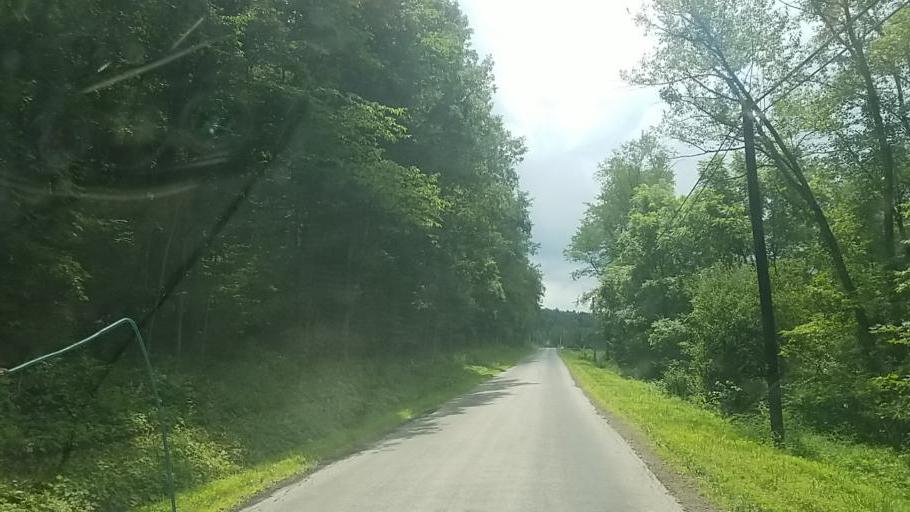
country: US
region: Ohio
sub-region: Muskingum County
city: Frazeysburg
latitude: 40.2038
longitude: -82.2598
